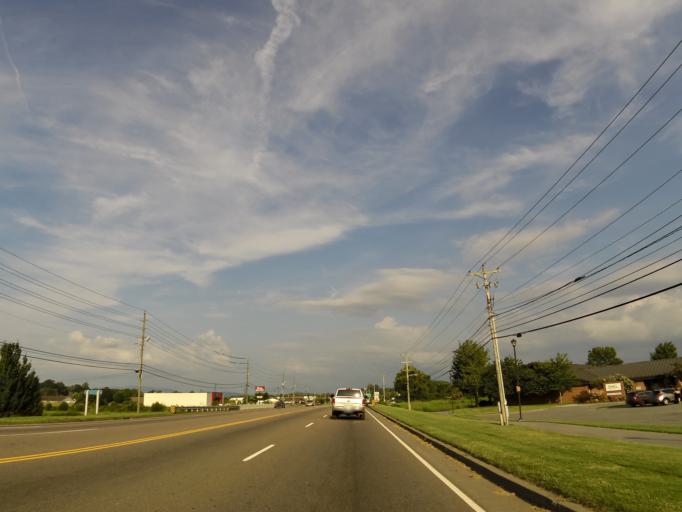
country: US
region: Tennessee
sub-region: Sevier County
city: Sevierville
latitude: 35.8671
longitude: -83.5578
